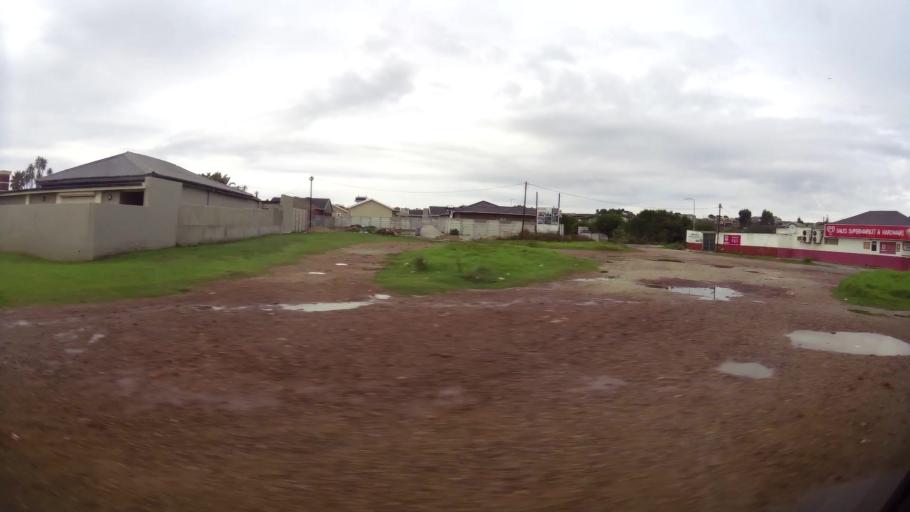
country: ZA
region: Eastern Cape
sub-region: Nelson Mandela Bay Metropolitan Municipality
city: Port Elizabeth
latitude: -33.9935
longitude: 25.5416
